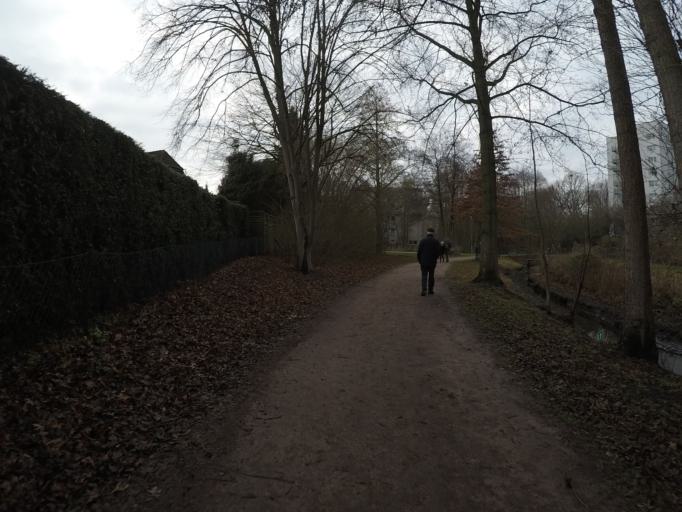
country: DE
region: Hamburg
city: Stellingen
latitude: 53.5951
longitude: 9.9506
